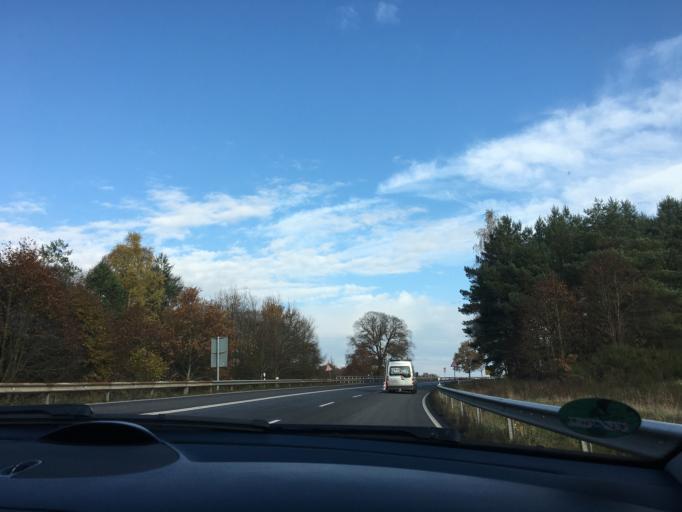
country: DE
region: Rheinland-Pfalz
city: Schopp
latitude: 49.3391
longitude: 7.6715
